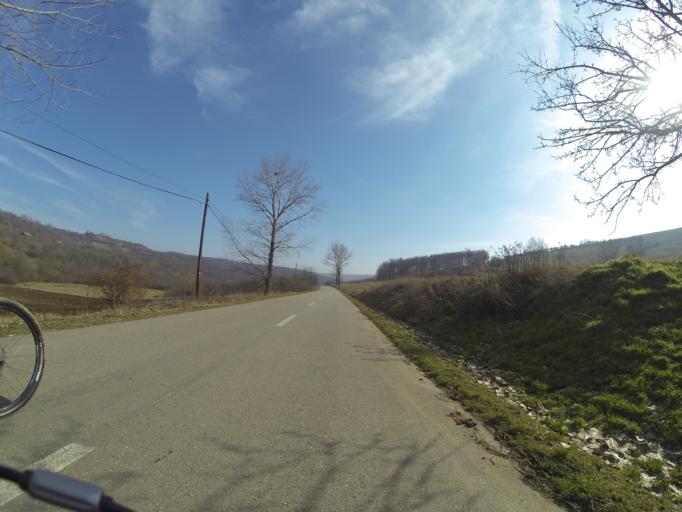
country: RO
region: Mehedinti
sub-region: Comuna Poroina Mare
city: Poroina Mare
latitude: 44.4941
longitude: 22.9293
